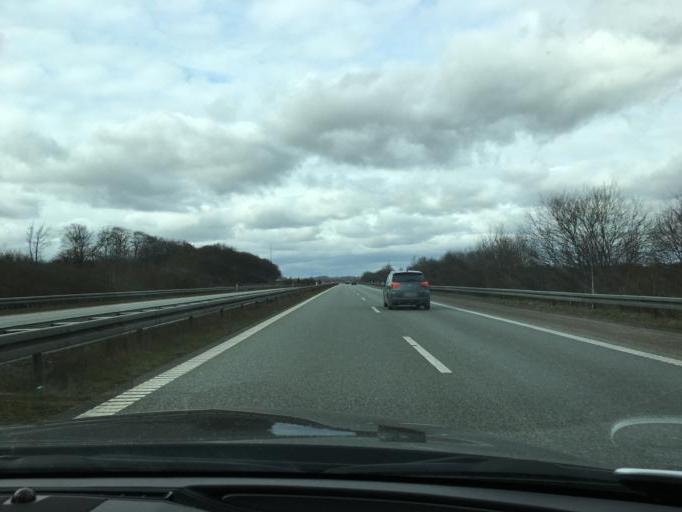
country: DK
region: South Denmark
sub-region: Vejen Kommune
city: Vejen
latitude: 55.4980
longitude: 9.0819
